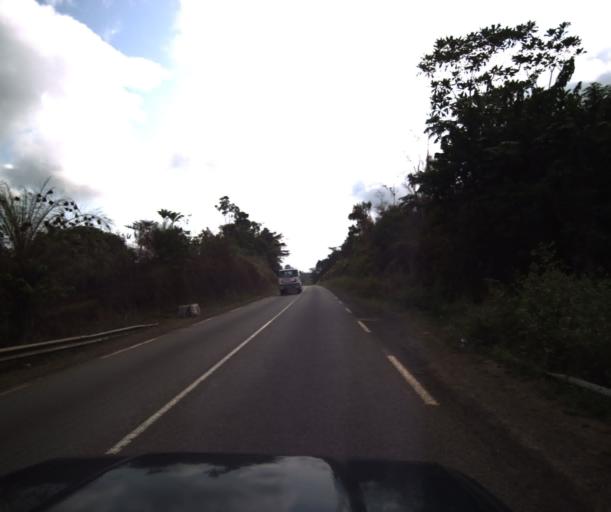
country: CM
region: Littoral
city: Edea
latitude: 3.7991
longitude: 10.2216
